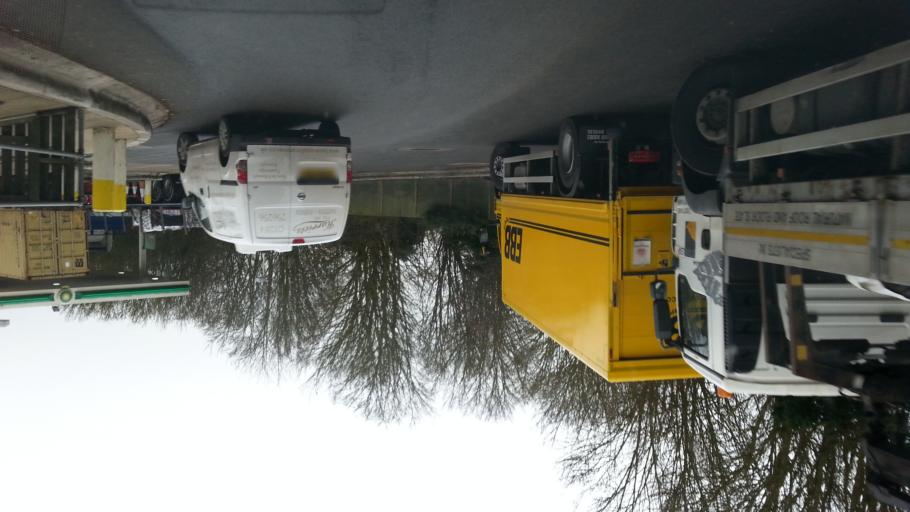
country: GB
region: England
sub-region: Suffolk
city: Exning
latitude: 52.2488
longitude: 0.3636
